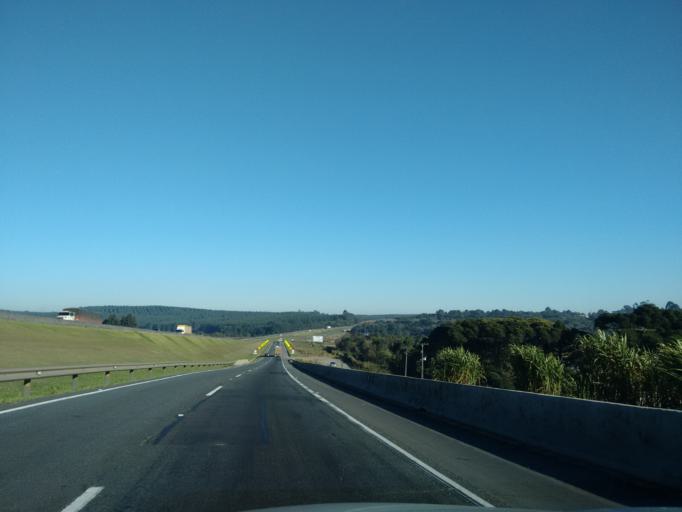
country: BR
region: Parana
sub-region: Campo Largo
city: Campo Largo
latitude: -25.4762
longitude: -49.7138
